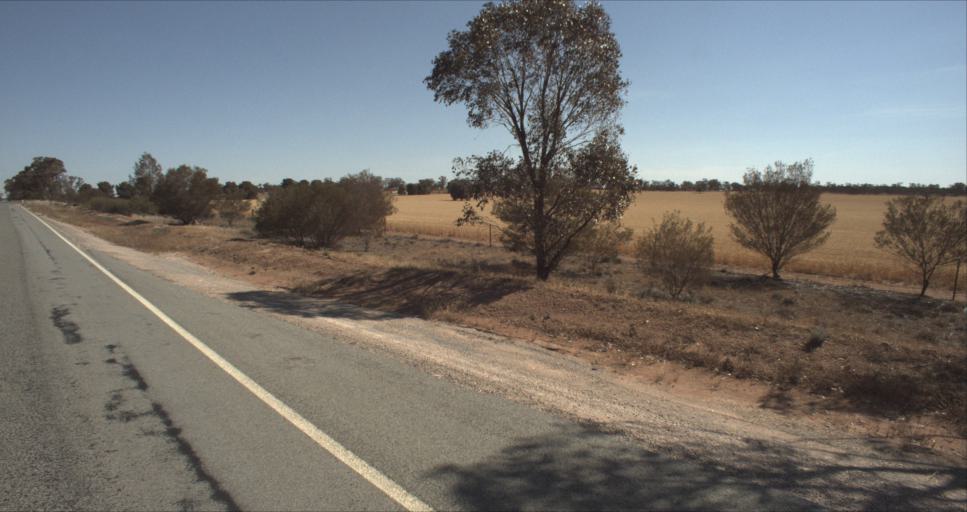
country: AU
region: New South Wales
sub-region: Leeton
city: Leeton
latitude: -34.4748
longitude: 146.4353
